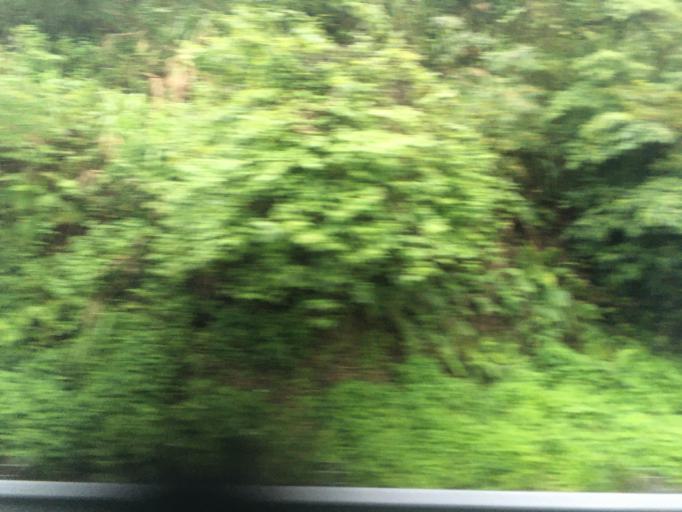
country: TW
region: Taipei
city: Taipei
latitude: 24.9822
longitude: 121.6639
